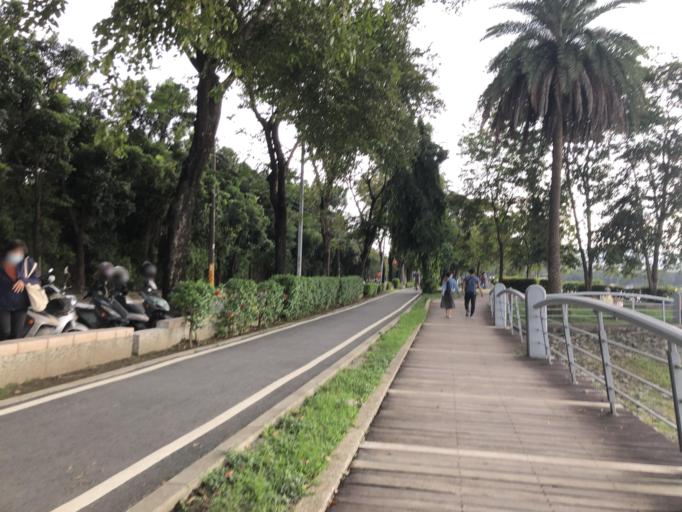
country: TW
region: Kaohsiung
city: Kaohsiung
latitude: 22.6821
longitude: 120.2980
